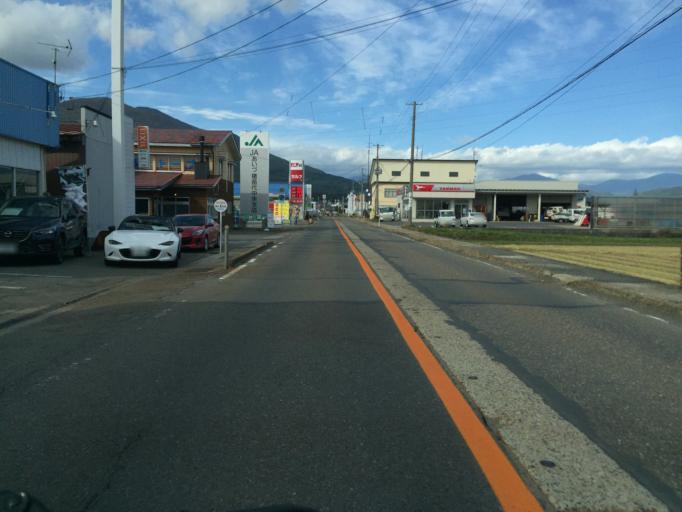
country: JP
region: Fukushima
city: Inawashiro
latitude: 37.5509
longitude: 140.1060
